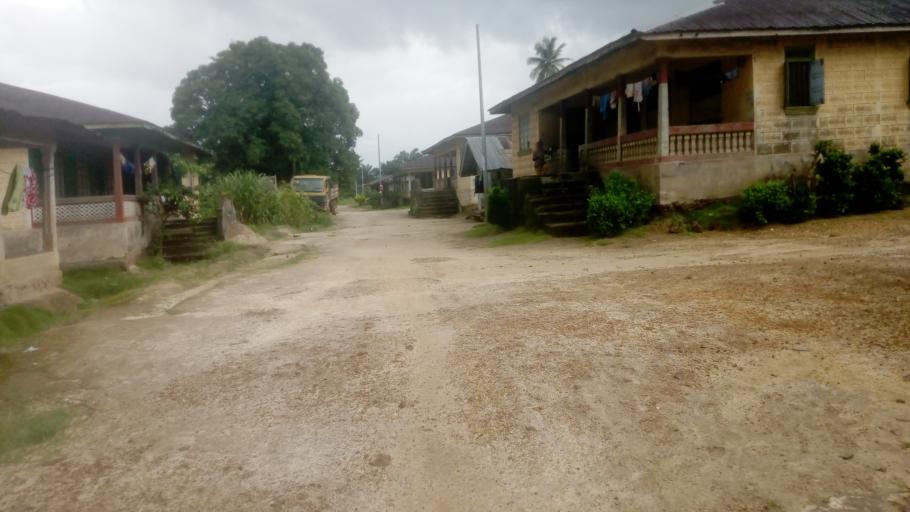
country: SL
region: Northern Province
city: Lunsar
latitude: 8.6839
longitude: -12.5413
